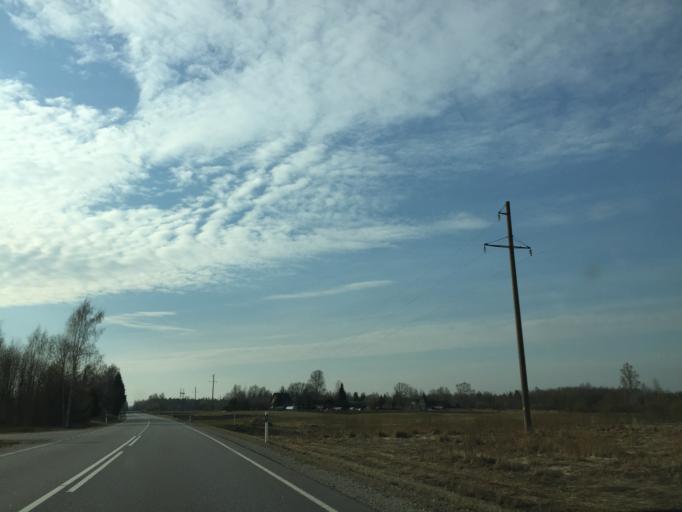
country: EE
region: Jogevamaa
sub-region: Mustvee linn
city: Mustvee
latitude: 58.8644
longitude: 26.8448
